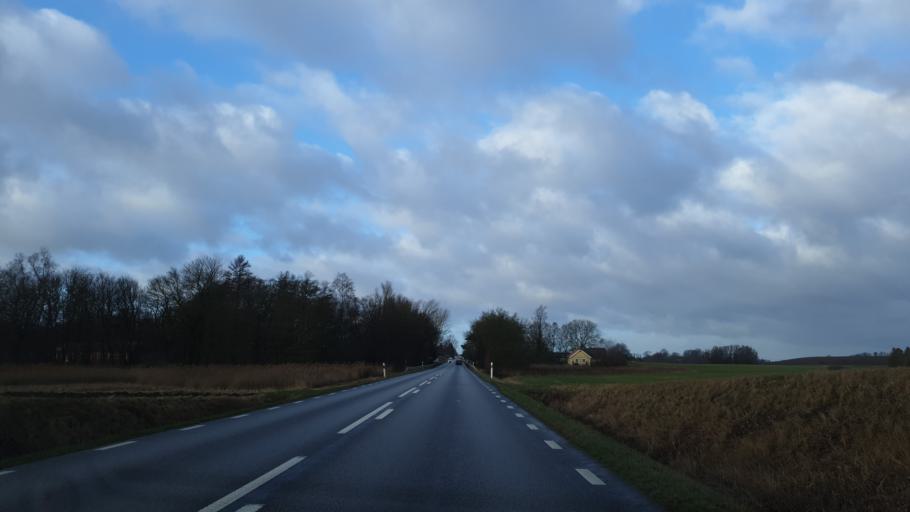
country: SE
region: Skane
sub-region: Malmo
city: Oxie
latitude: 55.4655
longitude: 13.1432
